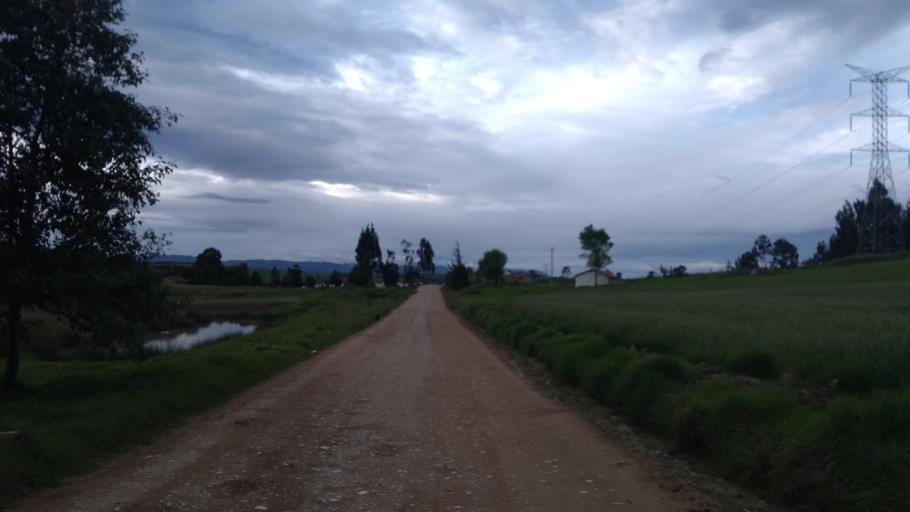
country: CO
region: Boyaca
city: Toca
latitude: 5.6016
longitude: -73.1791
